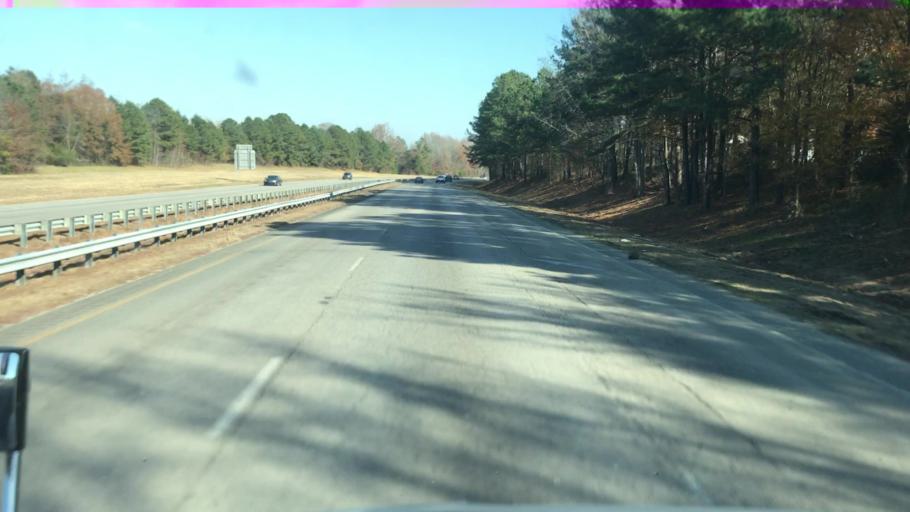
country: US
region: North Carolina
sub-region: Nash County
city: Nashville
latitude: 35.9746
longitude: -77.9335
